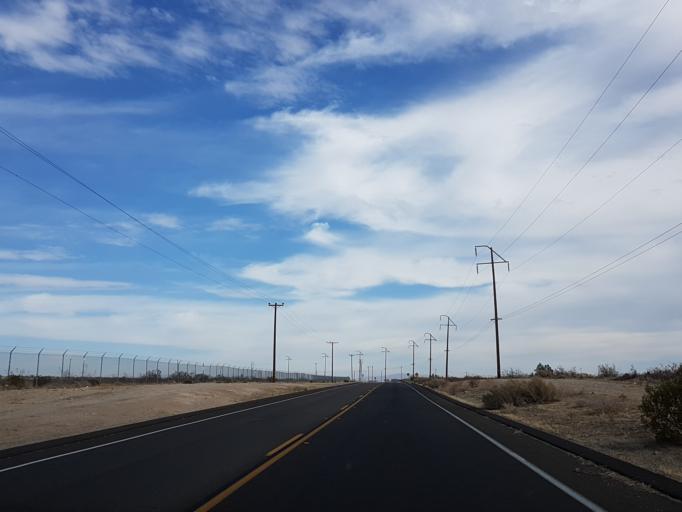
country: US
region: California
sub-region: Kern County
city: Ridgecrest
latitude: 35.6226
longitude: -117.6021
